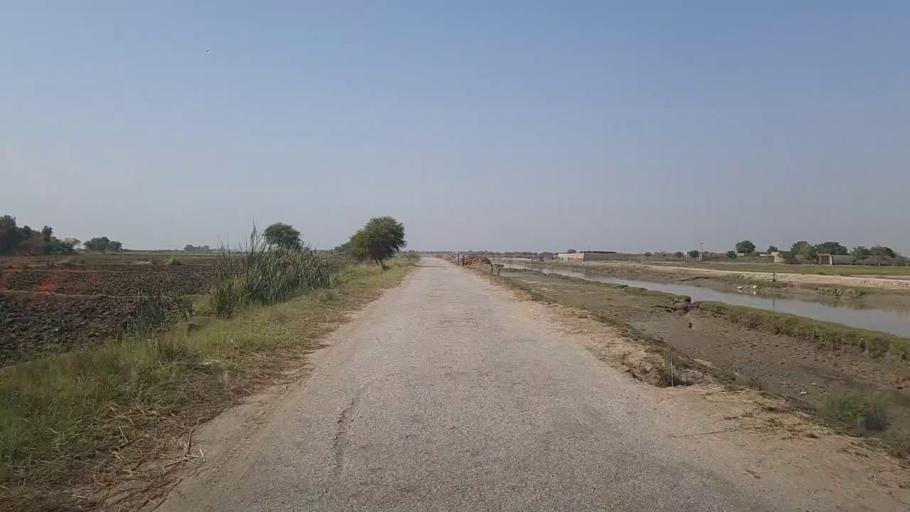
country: PK
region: Sindh
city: Kandhkot
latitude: 28.4139
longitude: 69.2386
